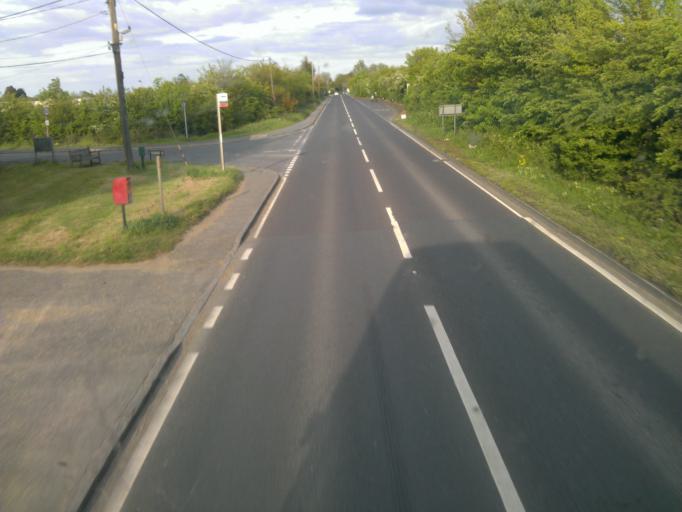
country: GB
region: England
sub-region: Essex
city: Marks Tey
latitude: 51.8766
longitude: 0.7441
